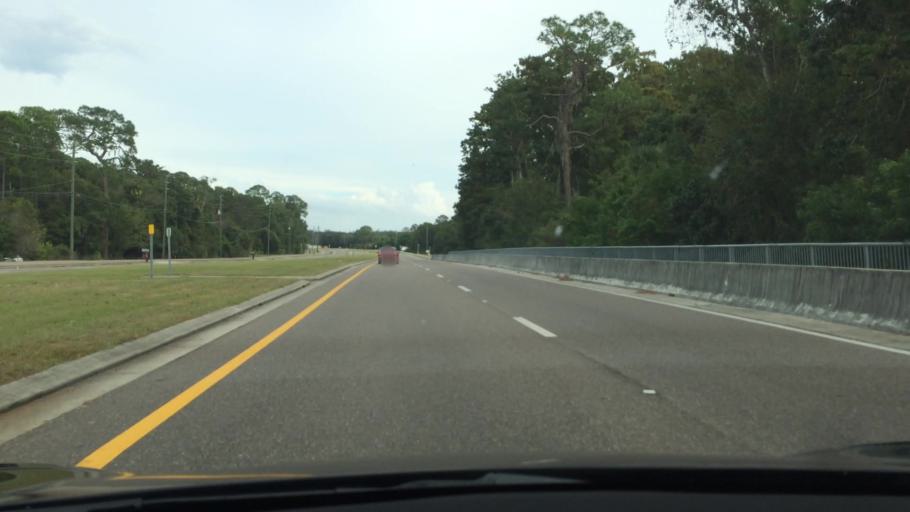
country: US
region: Florida
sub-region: Pinellas County
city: Tarpon Springs
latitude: 28.1528
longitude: -82.7200
